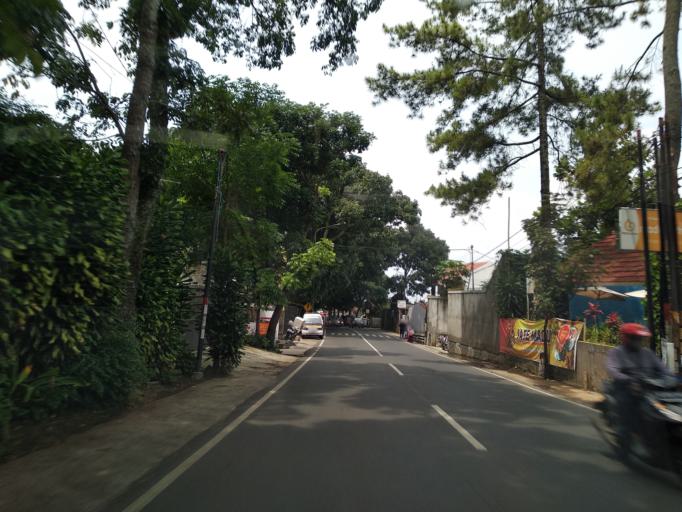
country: ID
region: West Java
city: Lembang
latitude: -6.8430
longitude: 107.5976
